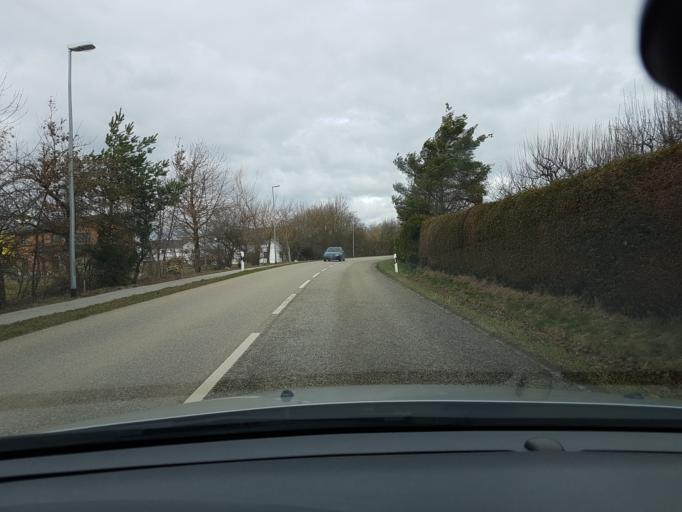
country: DE
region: Bavaria
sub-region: Lower Bavaria
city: Vilsbiburg
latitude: 48.4573
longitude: 12.3486
